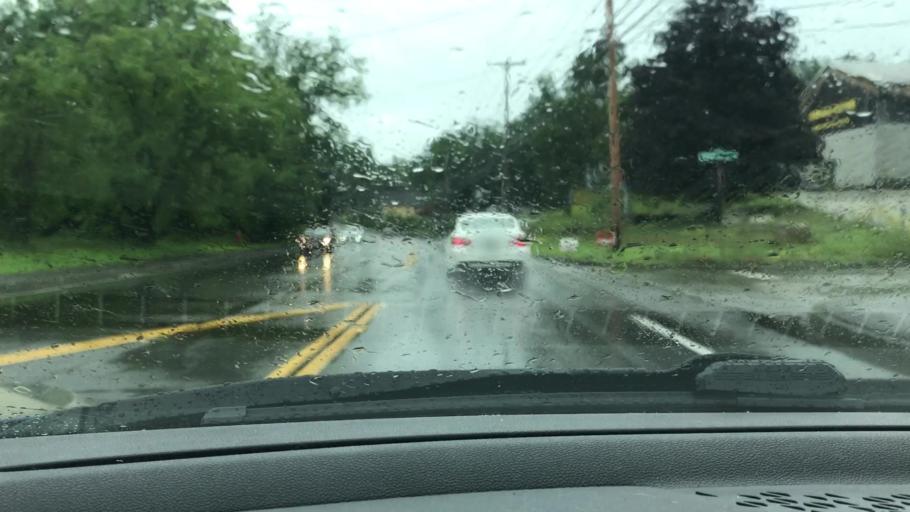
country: US
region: New Hampshire
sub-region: Merrimack County
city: East Concord
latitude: 43.2377
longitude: -71.5649
